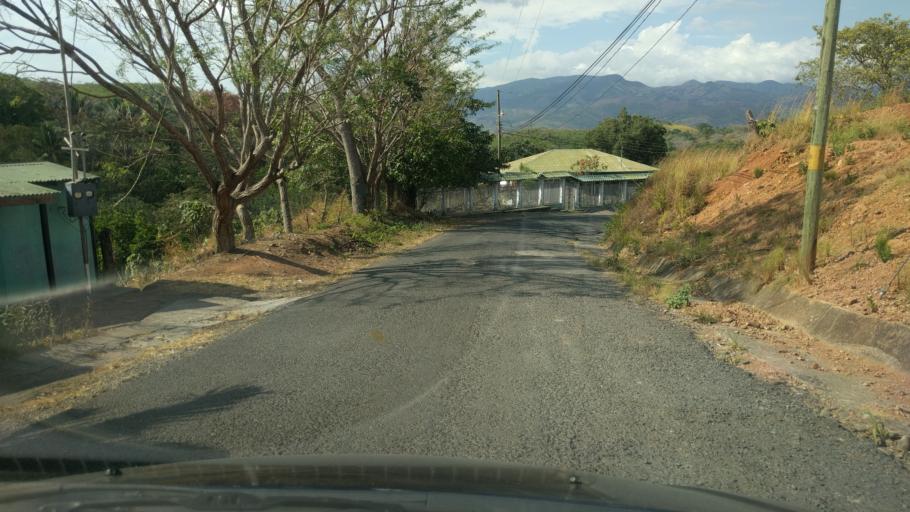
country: CR
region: Puntarenas
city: Esparza
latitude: 10.0140
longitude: -84.6953
